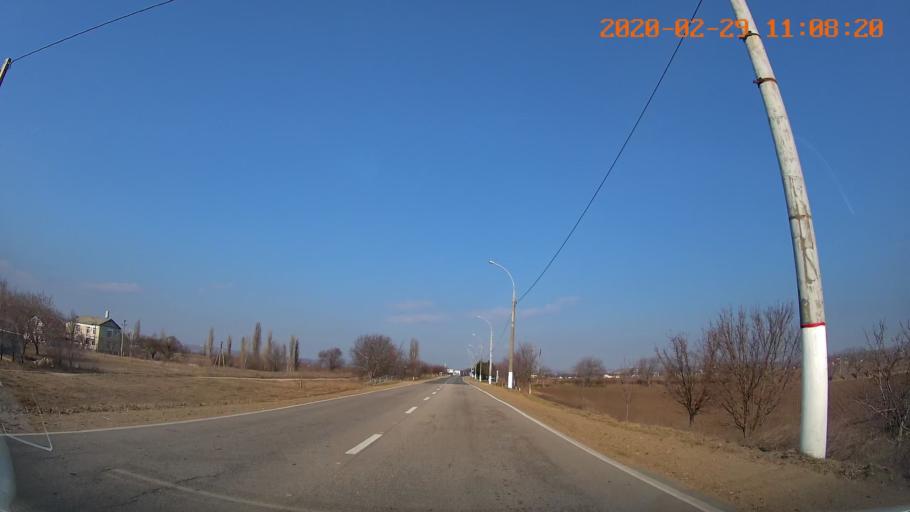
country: MD
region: Criuleni
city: Criuleni
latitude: 47.2330
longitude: 29.1763
